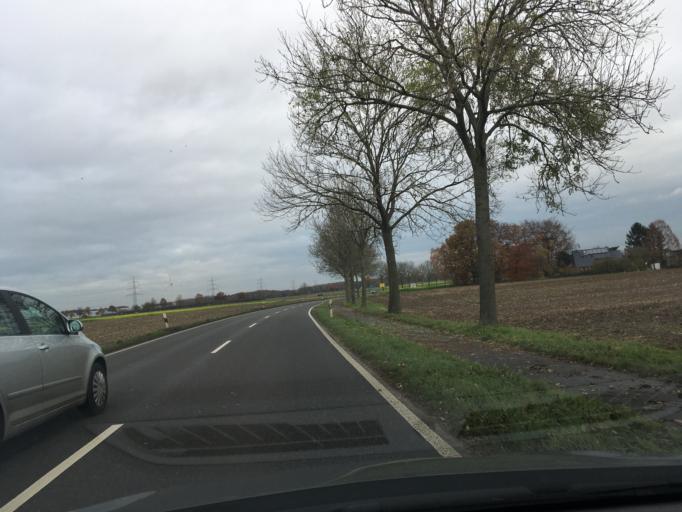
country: DE
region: North Rhine-Westphalia
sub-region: Regierungsbezirk Munster
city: Ahaus
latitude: 52.0915
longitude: 6.9651
